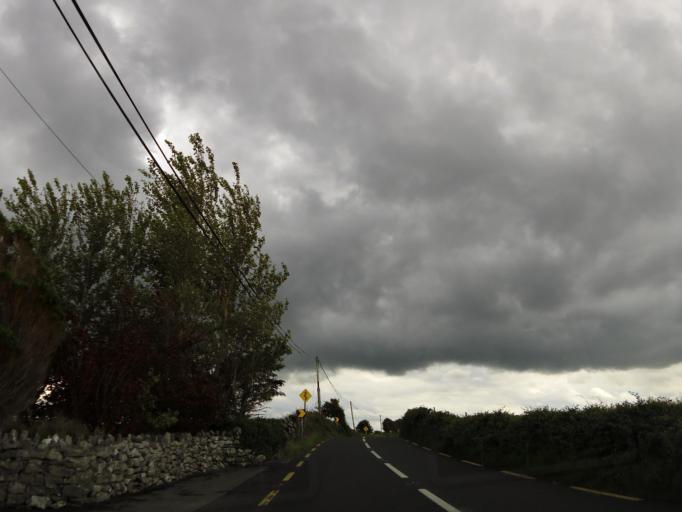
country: IE
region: Connaught
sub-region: County Galway
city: Oranmore
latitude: 53.1429
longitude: -8.9751
